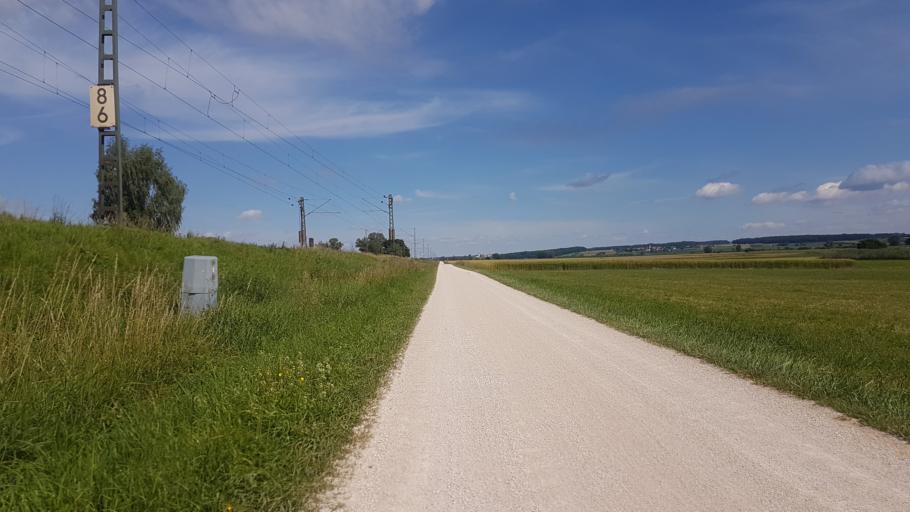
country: DE
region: Bavaria
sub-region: Regierungsbezirk Mittelfranken
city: Markt Berolzheim
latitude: 49.0216
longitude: 10.8496
